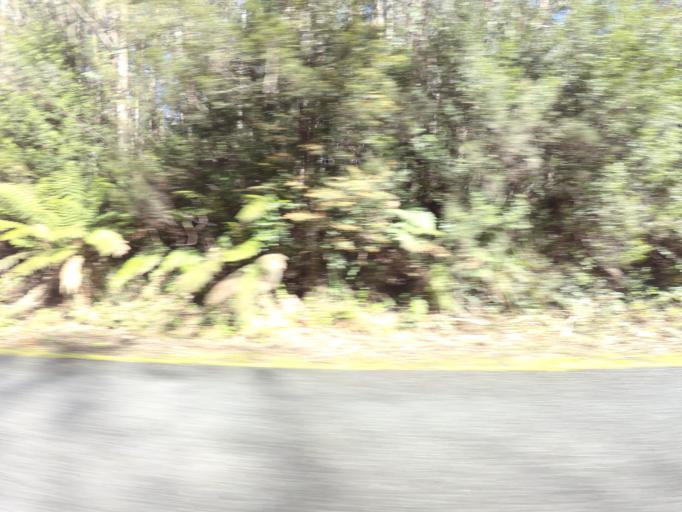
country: AU
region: Tasmania
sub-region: Derwent Valley
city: New Norfolk
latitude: -42.7503
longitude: 146.4122
